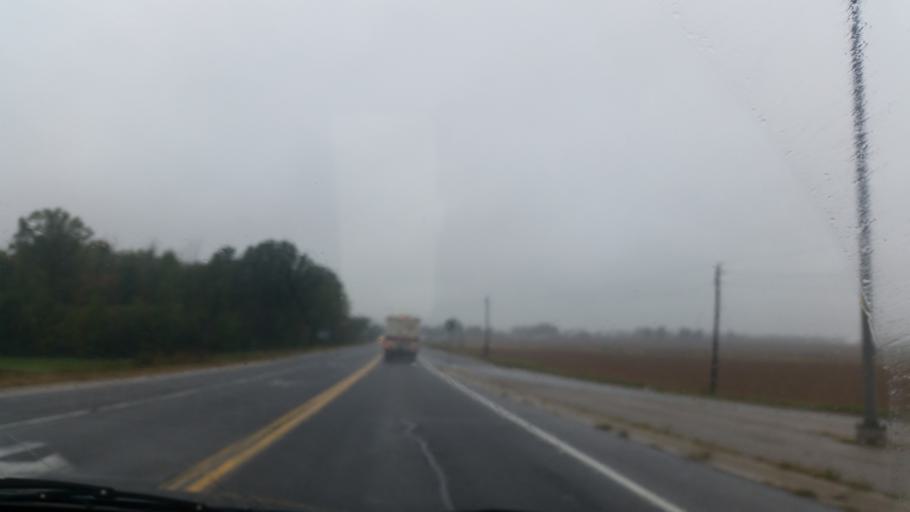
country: CA
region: Ontario
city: London
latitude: 43.1701
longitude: -81.3431
